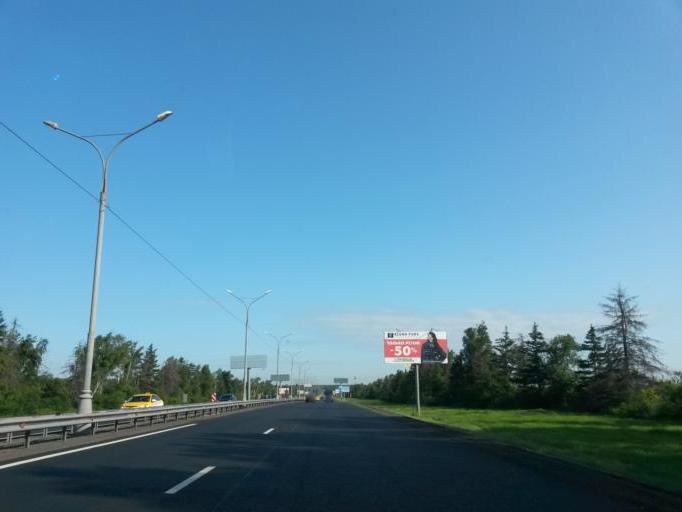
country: RU
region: Moskovskaya
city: Petrovskaya
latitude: 55.5243
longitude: 37.8198
